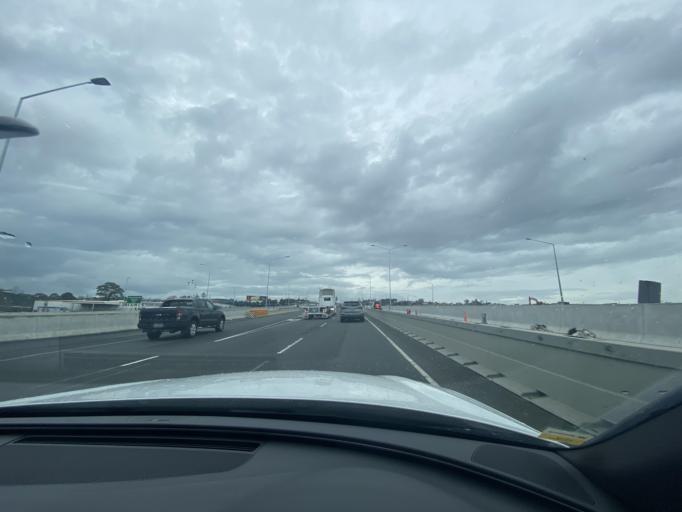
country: NZ
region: Auckland
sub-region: Auckland
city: Rothesay Bay
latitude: -36.7479
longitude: 174.7236
